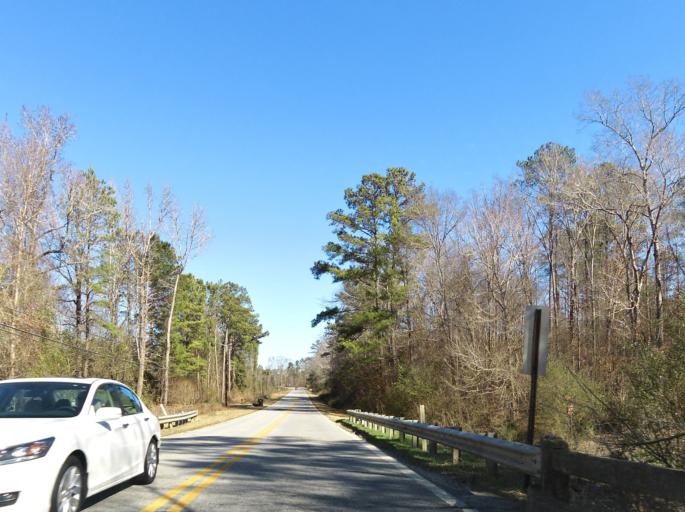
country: US
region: Georgia
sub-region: Bibb County
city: West Point
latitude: 32.8093
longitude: -83.7583
